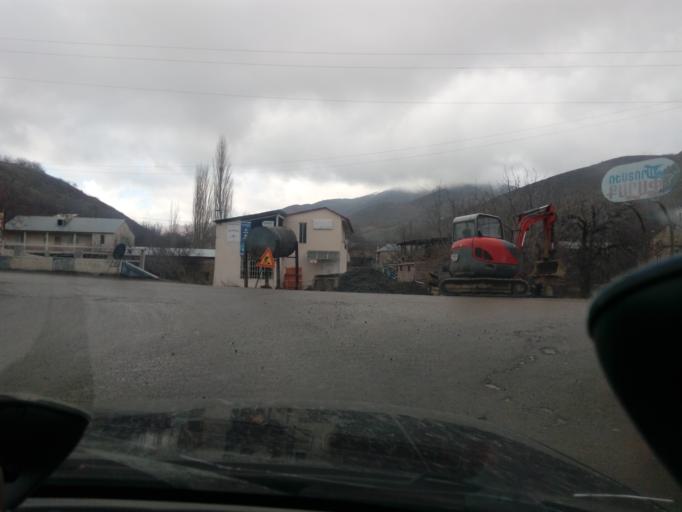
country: AM
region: Kotayk'i Marz
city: Arzakan
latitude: 40.4422
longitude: 44.6079
